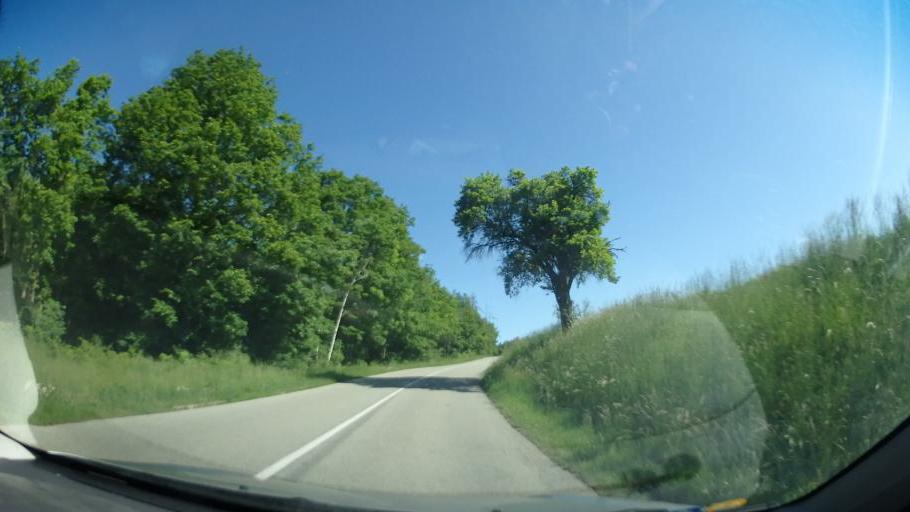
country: CZ
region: South Moravian
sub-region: Okres Blansko
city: Letovice
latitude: 49.5669
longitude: 16.5815
